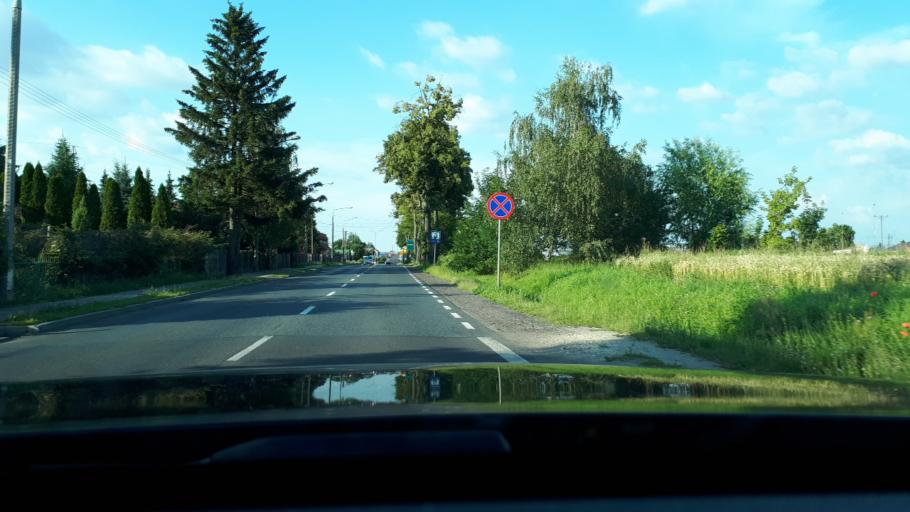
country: PL
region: Masovian Voivodeship
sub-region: Powiat ciechanowski
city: Ciechanow
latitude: 52.8583
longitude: 20.6302
